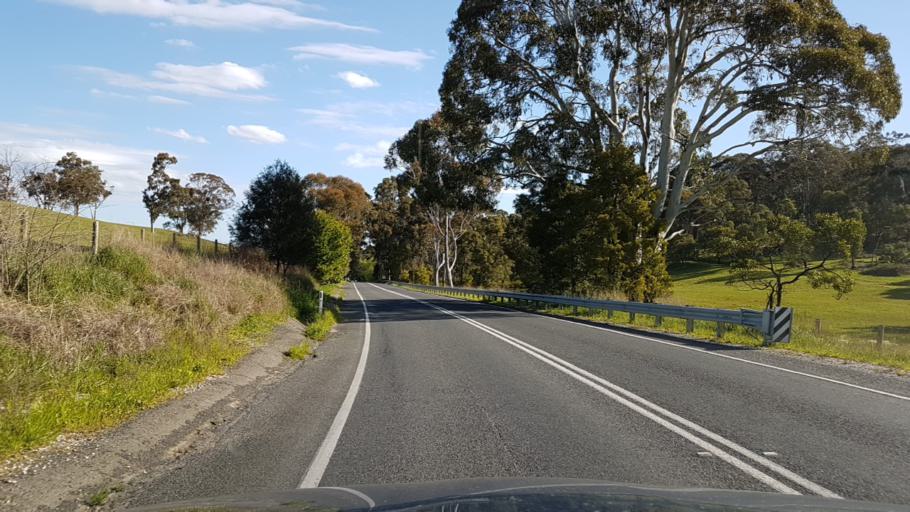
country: AU
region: South Australia
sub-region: Adelaide Hills
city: Lobethal
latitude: -34.8855
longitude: 138.8816
